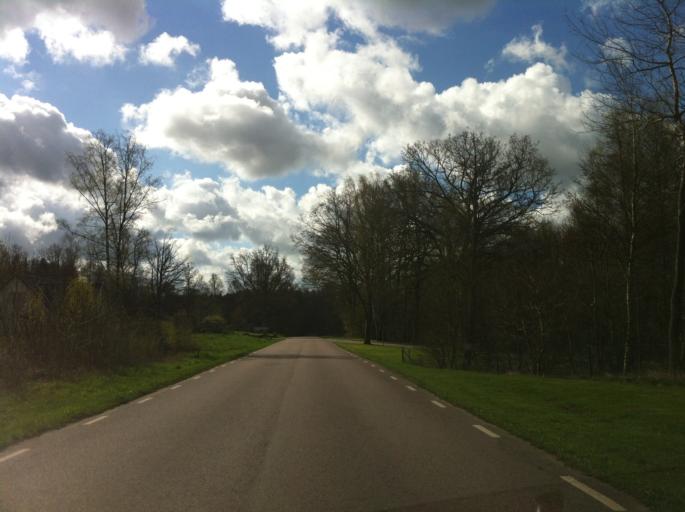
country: SE
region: Skane
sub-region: Hoors Kommun
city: Satofta
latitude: 55.8965
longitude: 13.6118
